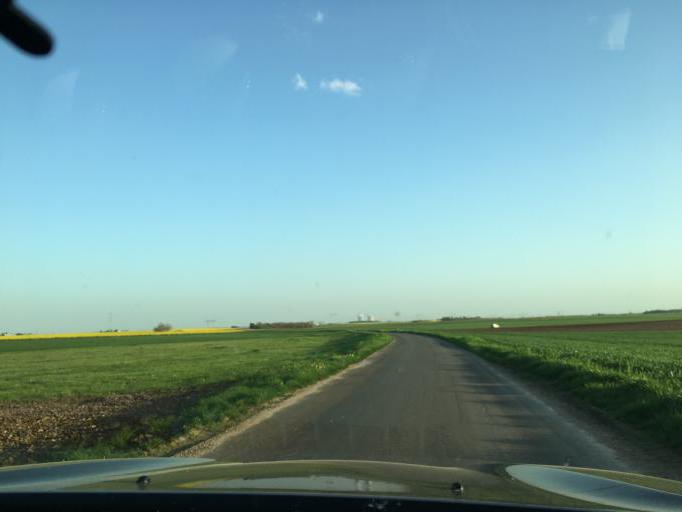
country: FR
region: Centre
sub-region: Departement du Loiret
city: Tavers
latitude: 47.7965
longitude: 1.5572
